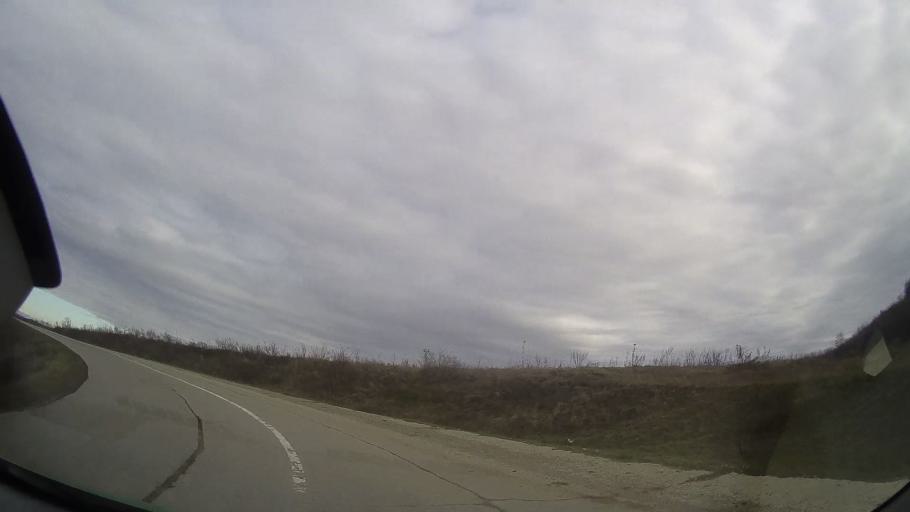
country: RO
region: Bistrita-Nasaud
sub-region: Comuna Micestii de Campie
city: Micestii de Campie
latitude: 46.8504
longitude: 24.3101
